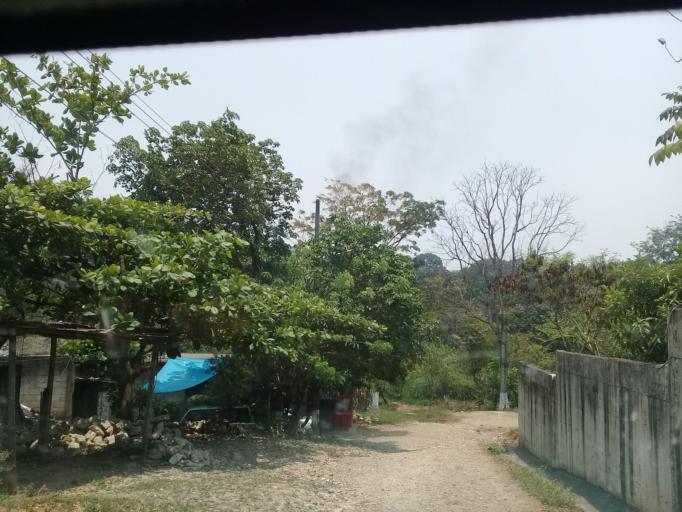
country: MX
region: Veracruz
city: Tezonapa
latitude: 18.6082
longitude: -96.6881
